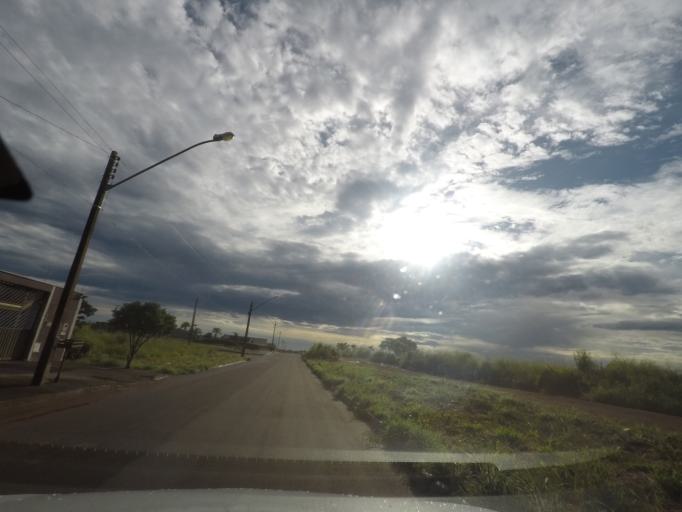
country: BR
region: Goias
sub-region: Aparecida De Goiania
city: Aparecida de Goiania
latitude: -16.7635
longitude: -49.3664
